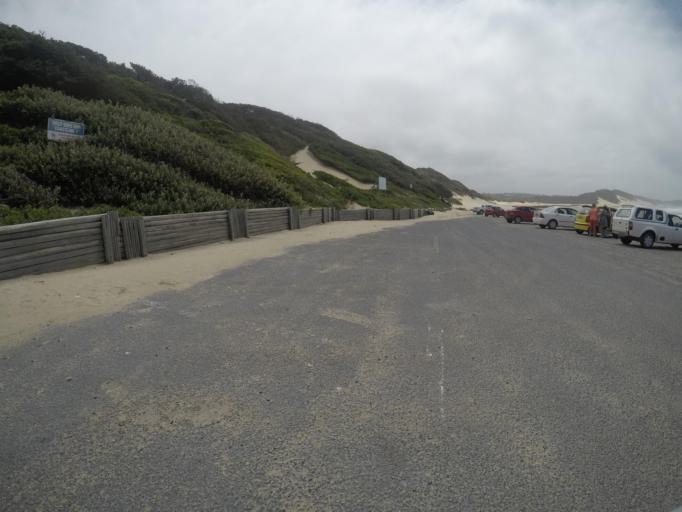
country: ZA
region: Eastern Cape
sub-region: Buffalo City Metropolitan Municipality
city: East London
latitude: -32.9931
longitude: 27.9484
